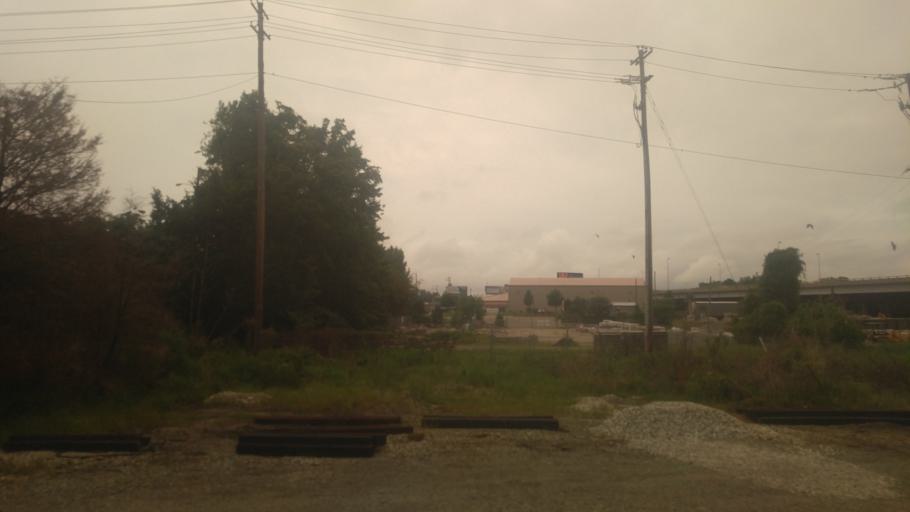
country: US
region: Virginia
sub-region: City of Richmond
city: Richmond
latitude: 37.5786
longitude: -77.4733
